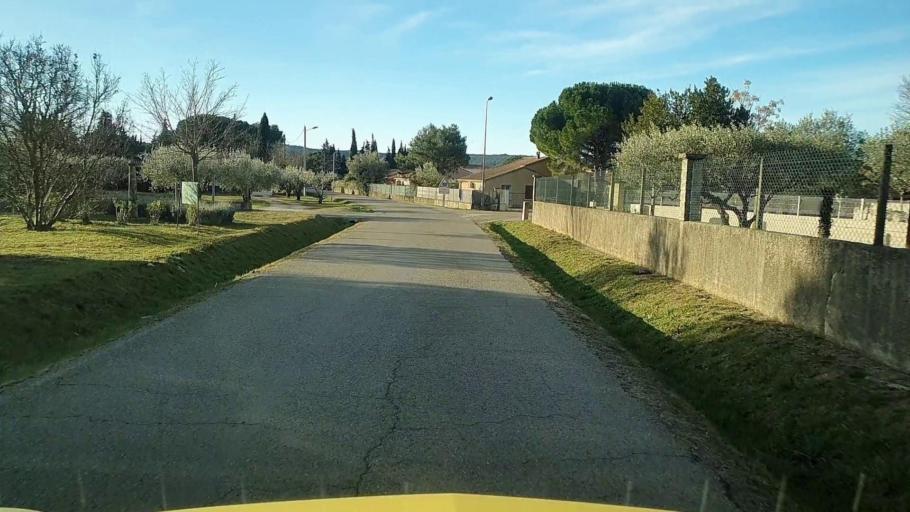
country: FR
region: Languedoc-Roussillon
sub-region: Departement du Gard
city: Castillon-du-Gard
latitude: 43.9586
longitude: 4.5517
